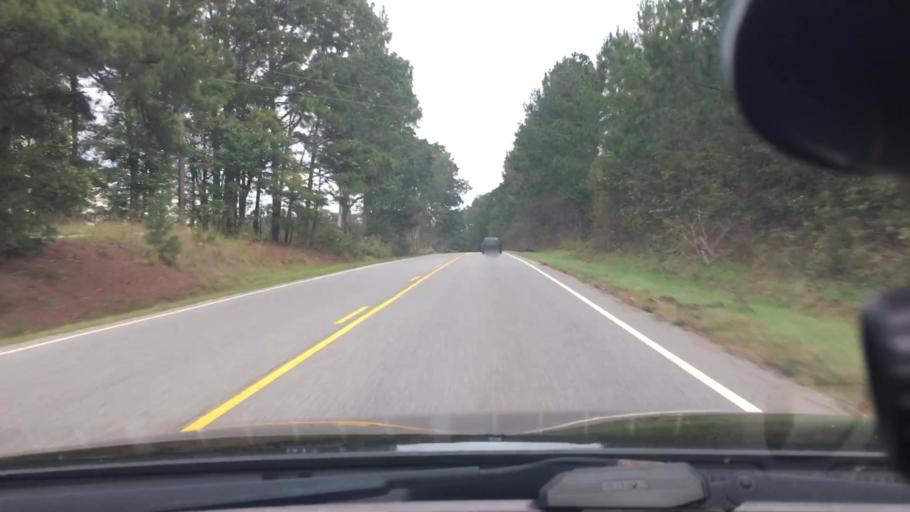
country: US
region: North Carolina
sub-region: Montgomery County
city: Biscoe
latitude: 35.3610
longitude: -79.6984
